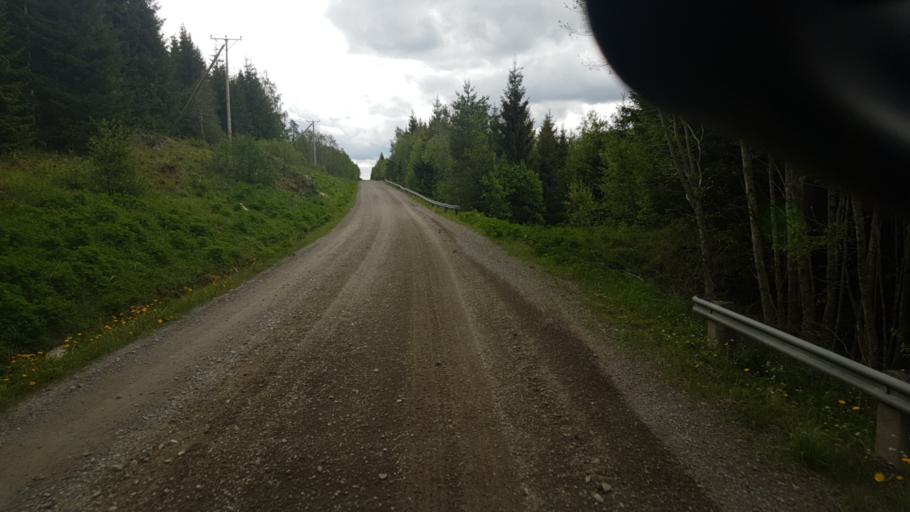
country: SE
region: Vaermland
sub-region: Arvika Kommun
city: Arvika
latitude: 59.8534
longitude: 12.7174
